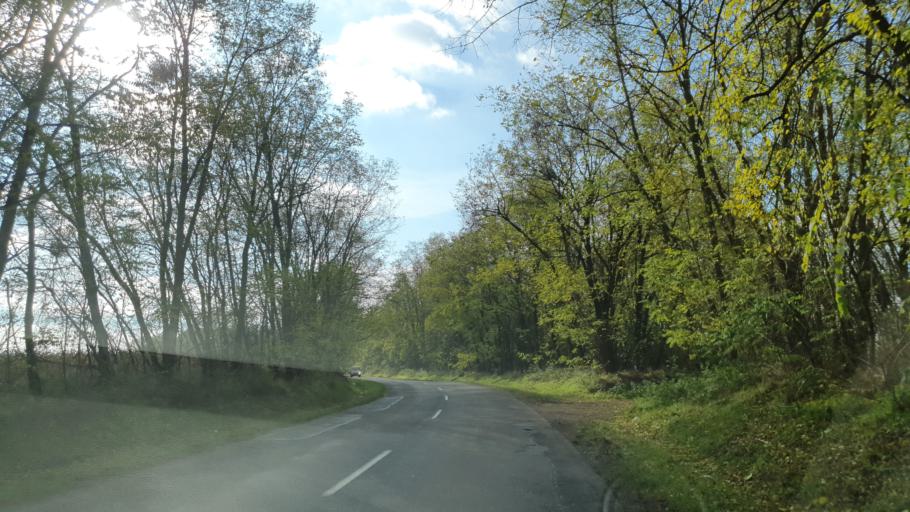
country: HU
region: Szabolcs-Szatmar-Bereg
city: Anarcs
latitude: 48.1585
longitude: 22.0943
